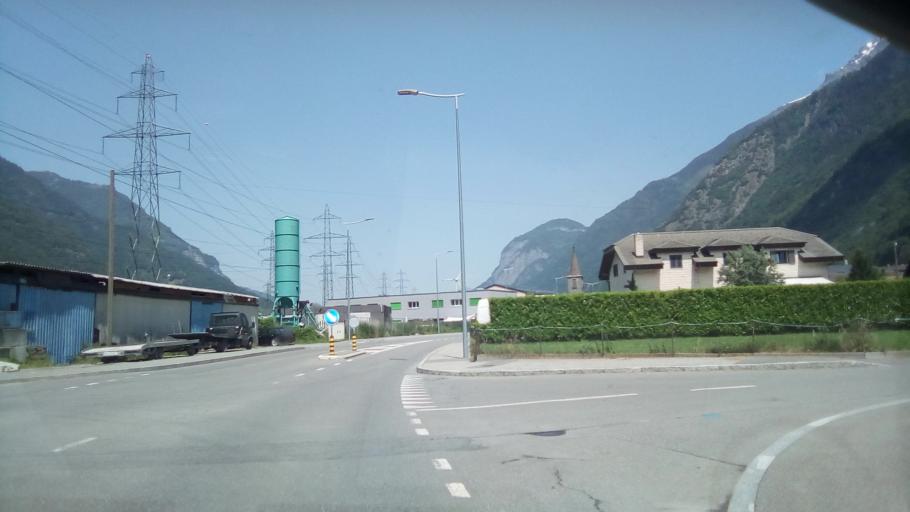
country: CH
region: Valais
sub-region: Saint-Maurice District
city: Vernayaz
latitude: 46.1465
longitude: 7.0422
